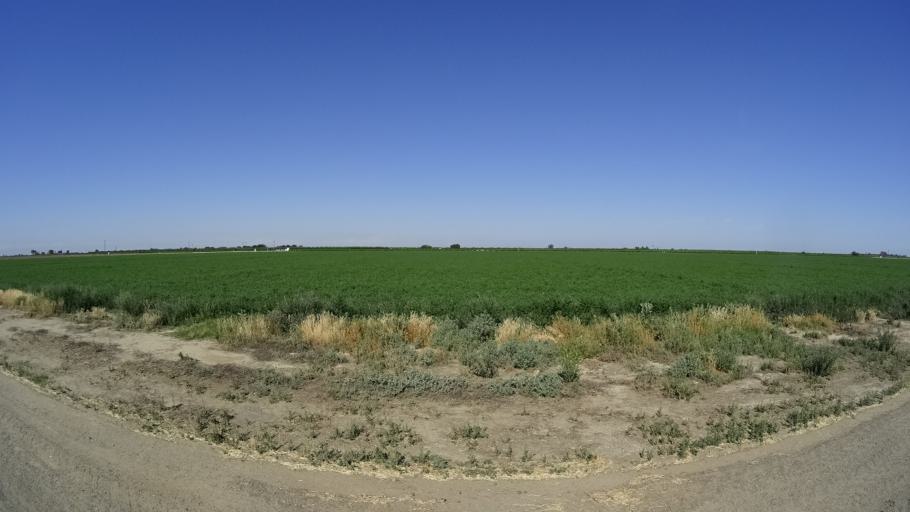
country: US
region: California
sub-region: Kings County
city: Home Garden
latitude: 36.2642
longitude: -119.5474
